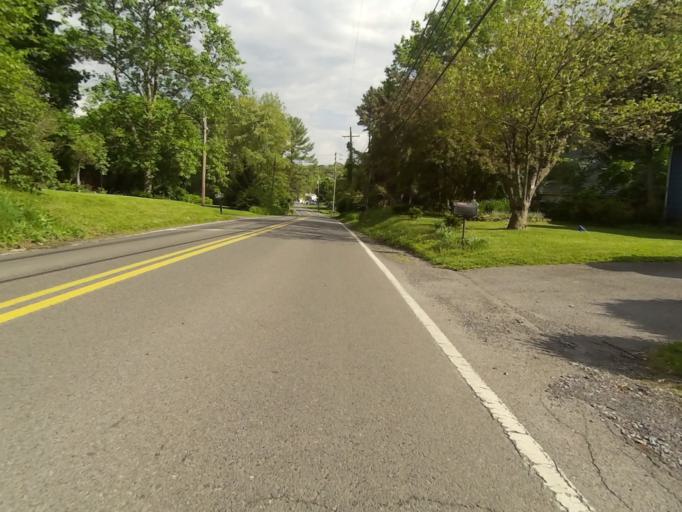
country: US
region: Pennsylvania
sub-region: Centre County
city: Houserville
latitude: 40.8230
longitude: -77.8283
